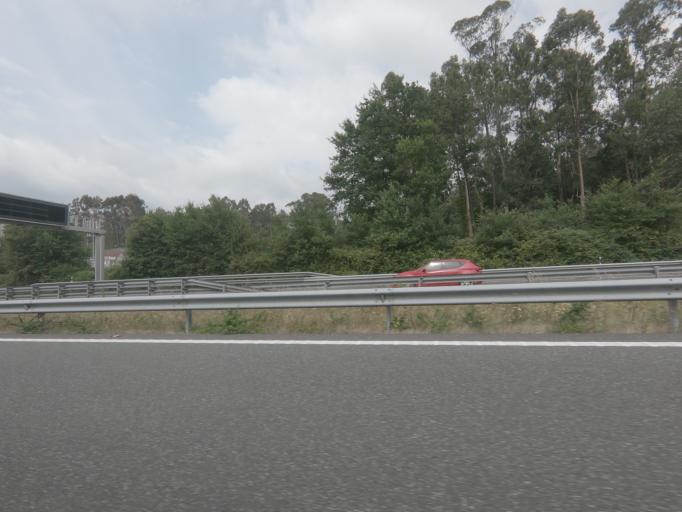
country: ES
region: Galicia
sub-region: Provincia de Pontevedra
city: Ponteareas
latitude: 42.1502
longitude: -8.4784
